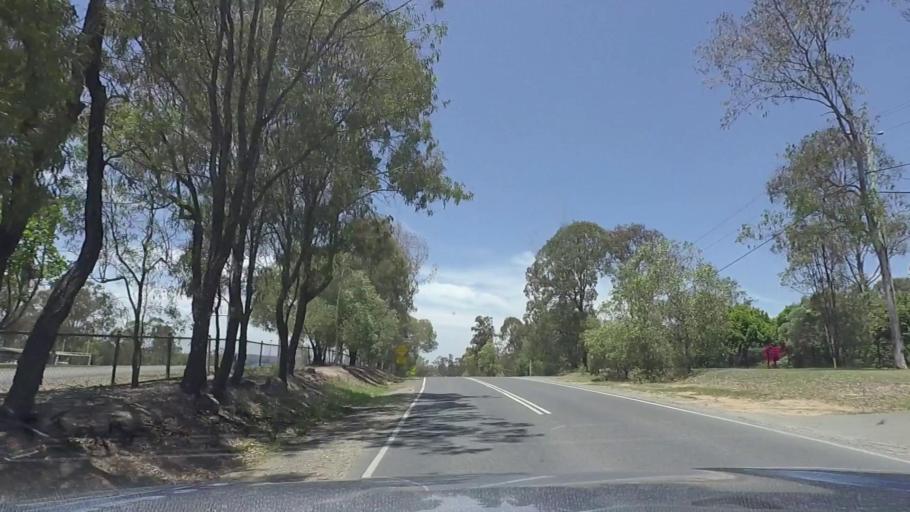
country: AU
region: Queensland
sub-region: Logan
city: North Maclean
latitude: -27.8271
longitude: 153.0251
